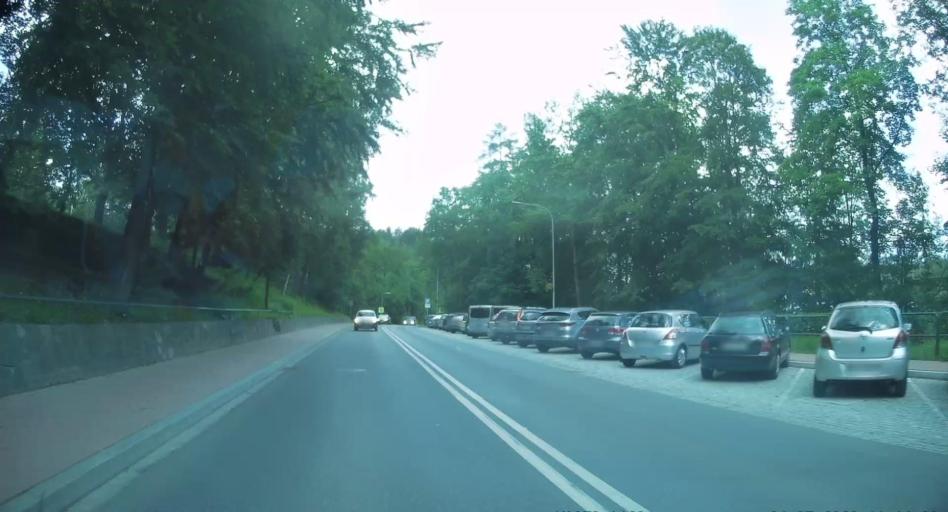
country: PL
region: Lesser Poland Voivodeship
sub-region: Powiat nowosadecki
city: Krynica-Zdroj
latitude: 49.4164
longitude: 20.9553
